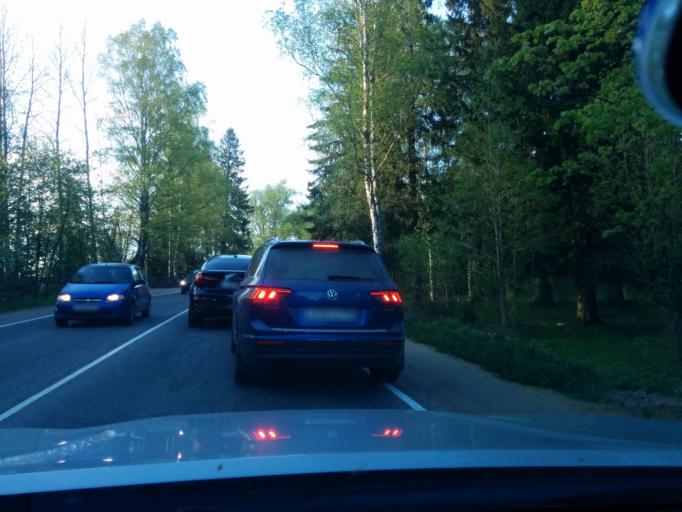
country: RU
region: Leningrad
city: Verkhniye Osel'ki
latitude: 60.2313
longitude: 30.4323
